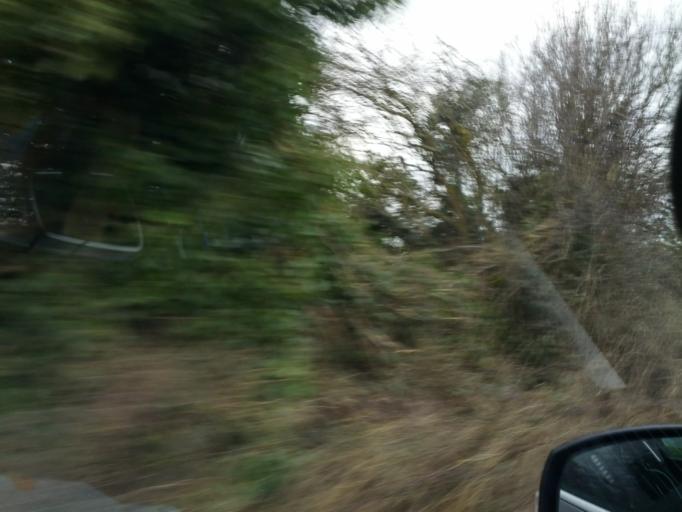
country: IE
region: Connaught
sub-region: County Galway
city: Gort
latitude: 53.1766
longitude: -8.8449
